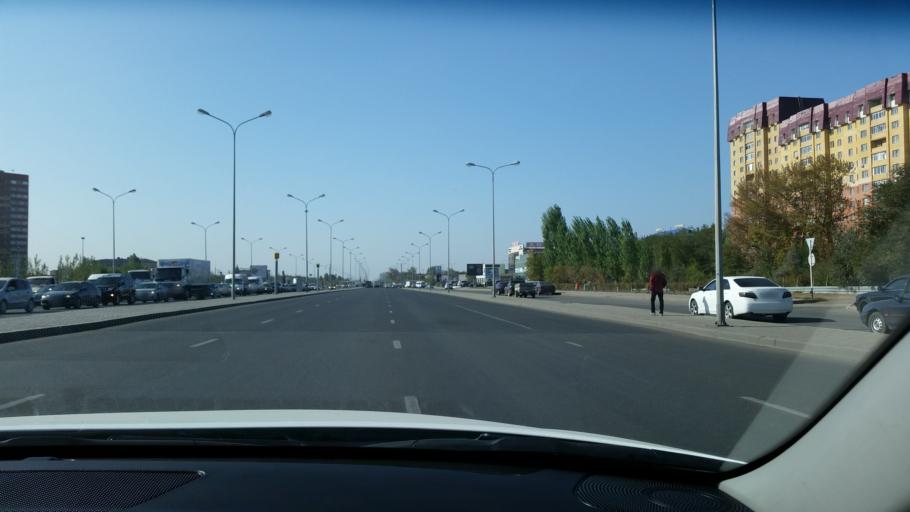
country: KZ
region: Astana Qalasy
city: Astana
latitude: 51.1803
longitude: 71.3799
